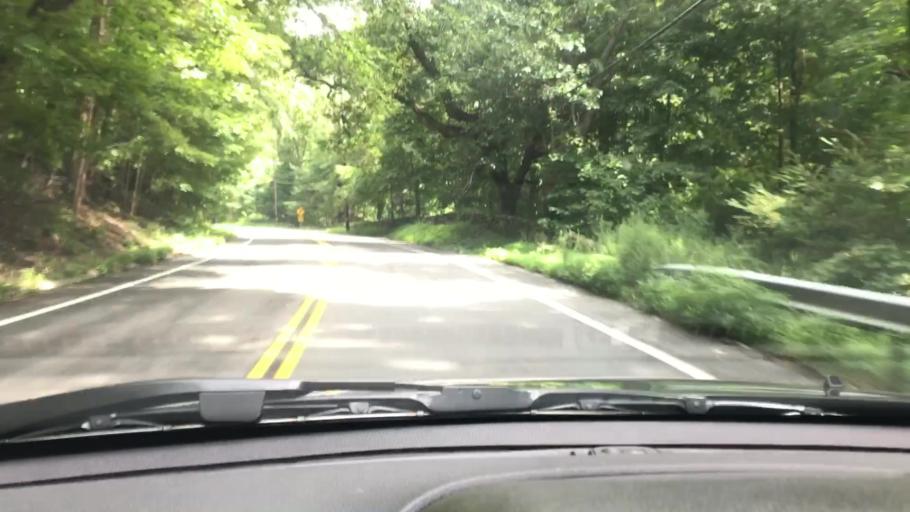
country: US
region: New York
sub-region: Westchester County
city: Bedford
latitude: 41.2200
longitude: -73.6654
